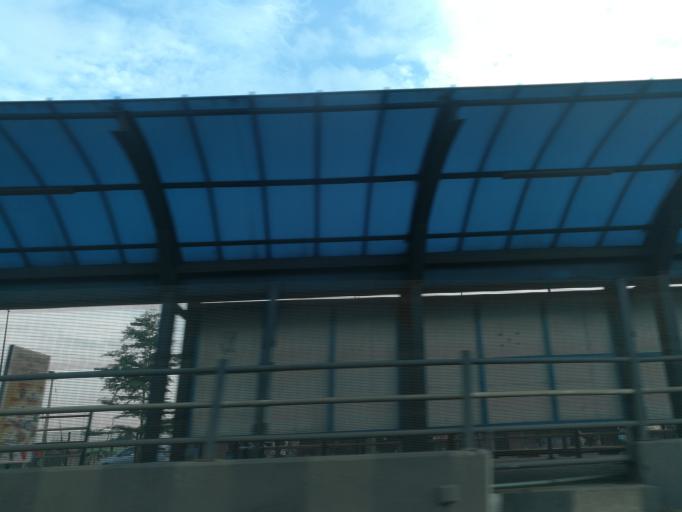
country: NG
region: Lagos
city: Ebute Ikorodu
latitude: 6.6198
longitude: 3.4724
